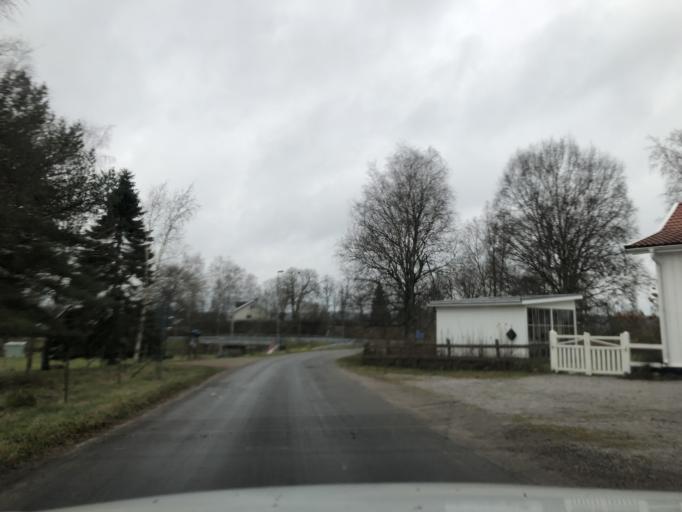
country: SE
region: Vaestra Goetaland
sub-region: Ulricehamns Kommun
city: Ulricehamn
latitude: 57.8622
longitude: 13.5552
